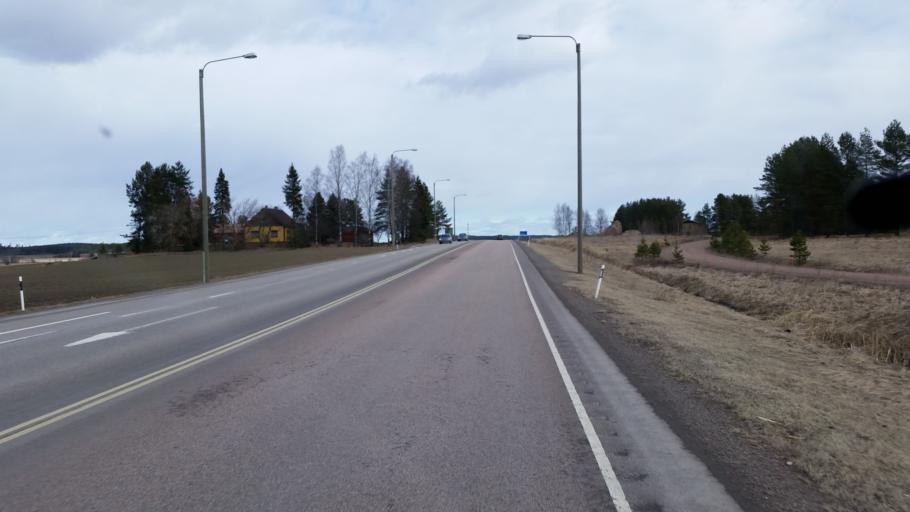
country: FI
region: Kymenlaakso
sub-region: Kouvola
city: Elimaeki
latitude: 60.7338
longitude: 26.4365
